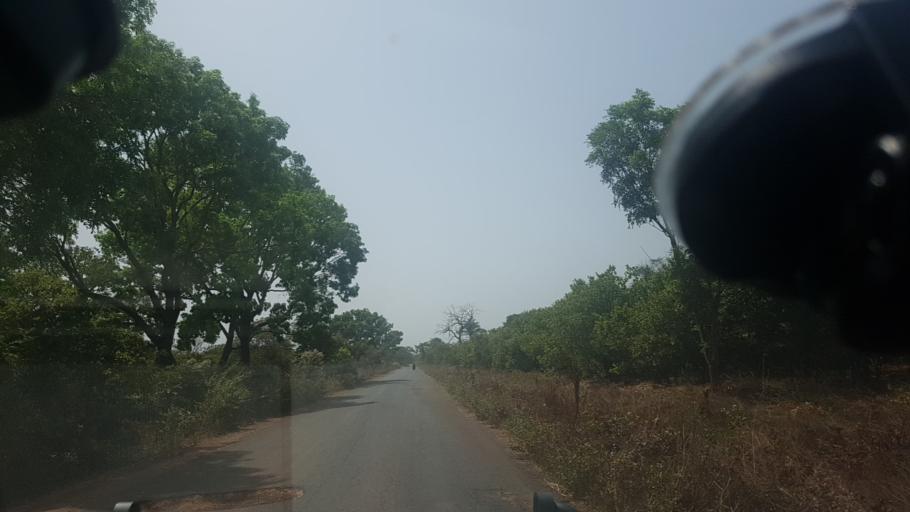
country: GW
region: Cacheu
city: Cacheu
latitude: 12.4098
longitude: -16.0347
